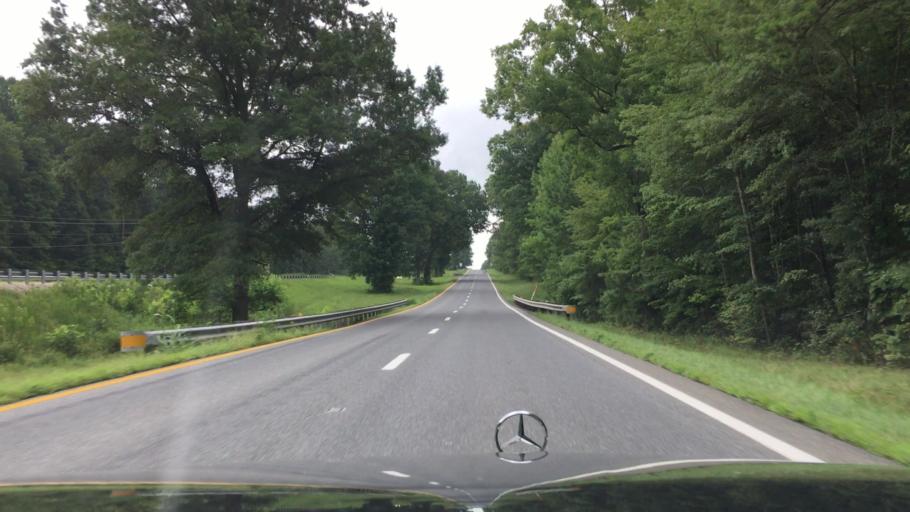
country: US
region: Virginia
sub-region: Appomattox County
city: Appomattox
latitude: 37.3059
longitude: -78.7507
